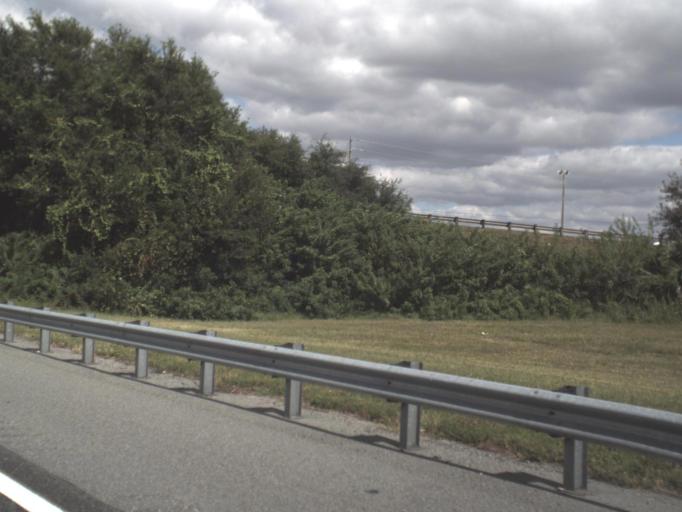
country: US
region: Florida
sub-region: Orange County
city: Southchase
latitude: 28.4208
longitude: -81.3934
